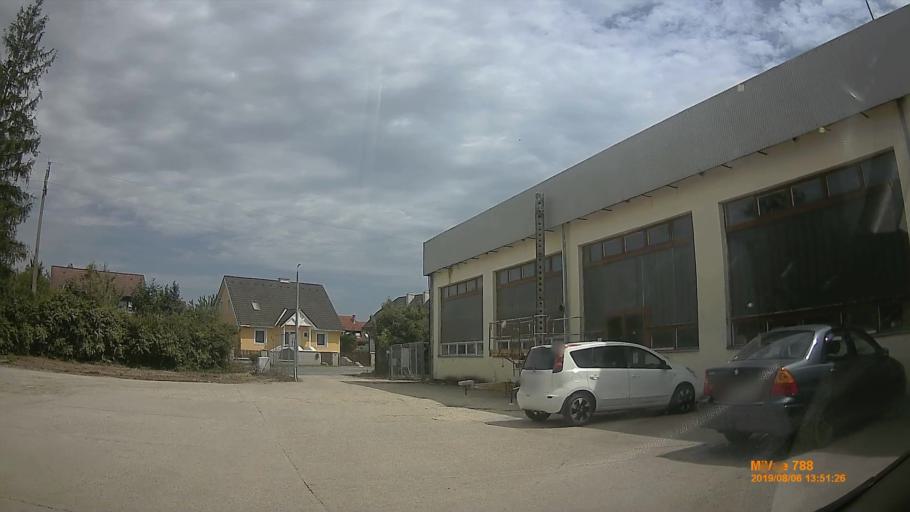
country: HU
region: Vas
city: Szombathely
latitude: 47.2516
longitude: 16.6010
